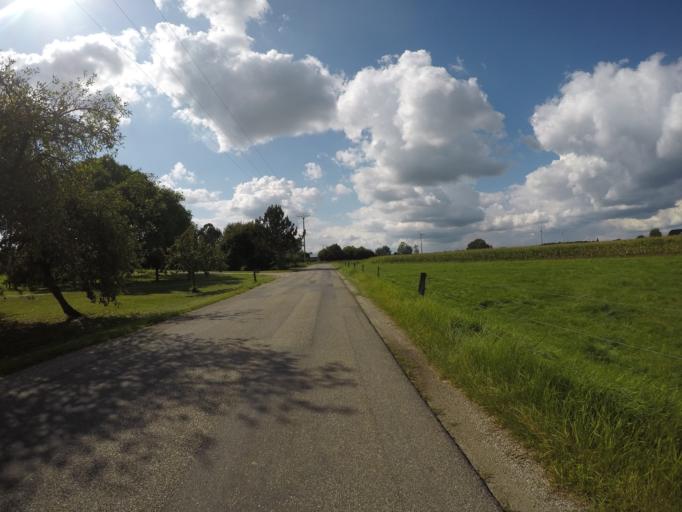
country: DE
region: North Rhine-Westphalia
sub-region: Regierungsbezirk Dusseldorf
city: Mehrhoog
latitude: 51.7696
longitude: 6.5220
